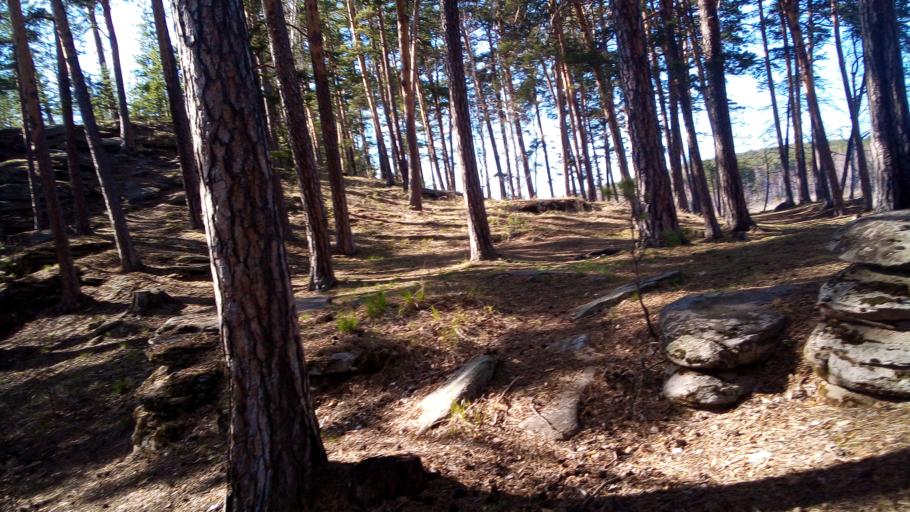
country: RU
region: Chelyabinsk
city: Chebarkul'
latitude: 55.1137
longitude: 60.3332
